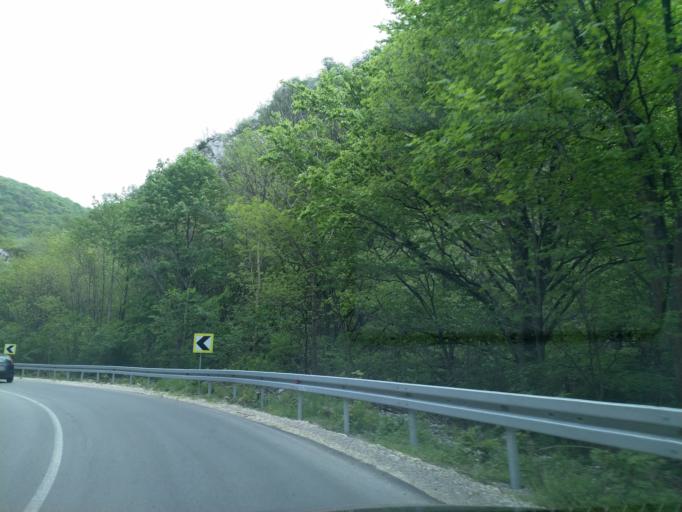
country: RS
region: Central Serbia
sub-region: Pomoravski Okrug
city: Despotovac
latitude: 43.9726
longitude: 21.5200
